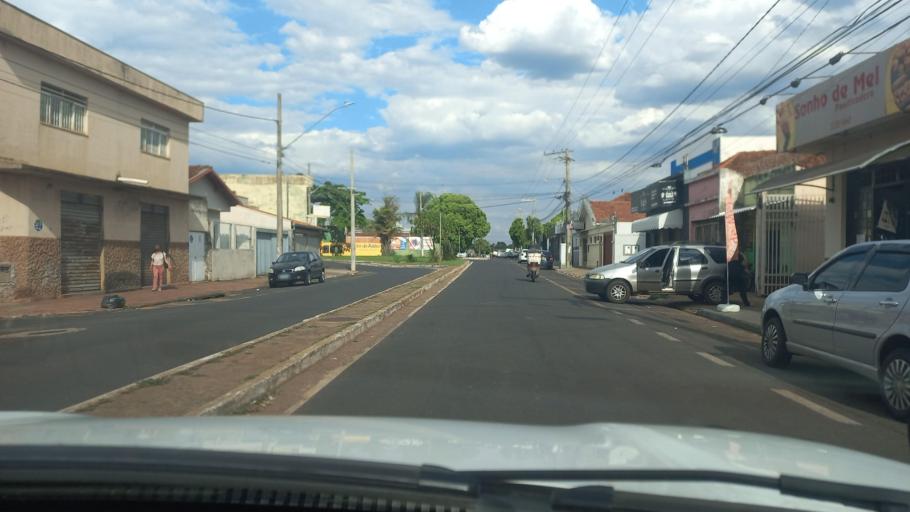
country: BR
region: Minas Gerais
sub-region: Uberaba
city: Uberaba
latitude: -19.7350
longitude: -47.9183
